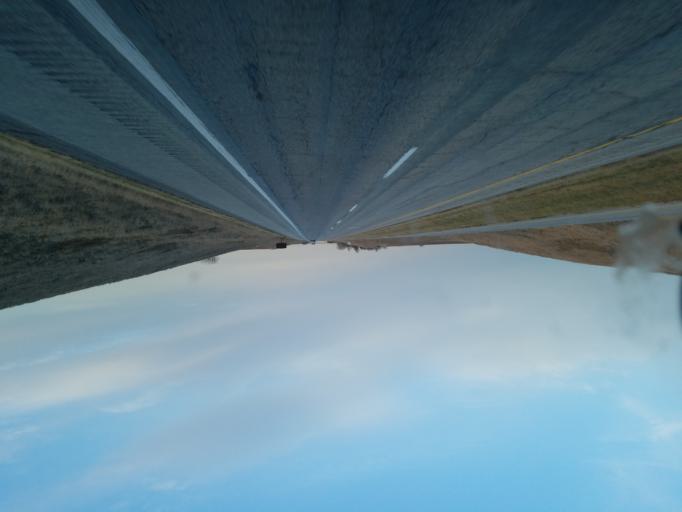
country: US
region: Iowa
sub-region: Harrison County
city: Missouri Valley
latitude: 41.4994
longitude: -95.7823
